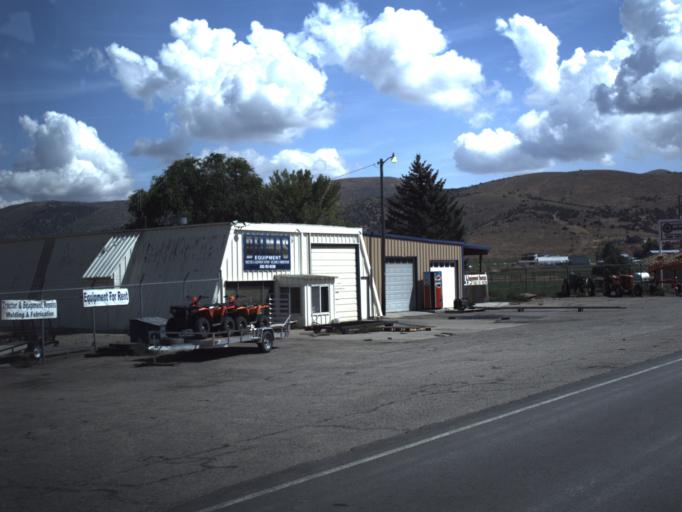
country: US
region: Utah
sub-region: Rich County
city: Randolph
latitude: 41.8323
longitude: -111.3244
